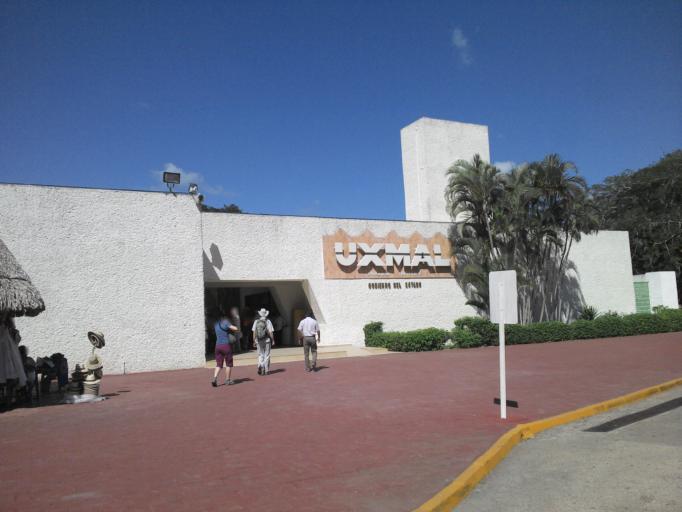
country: MX
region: Yucatan
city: Santa Elena
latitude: 20.3605
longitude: -89.7673
